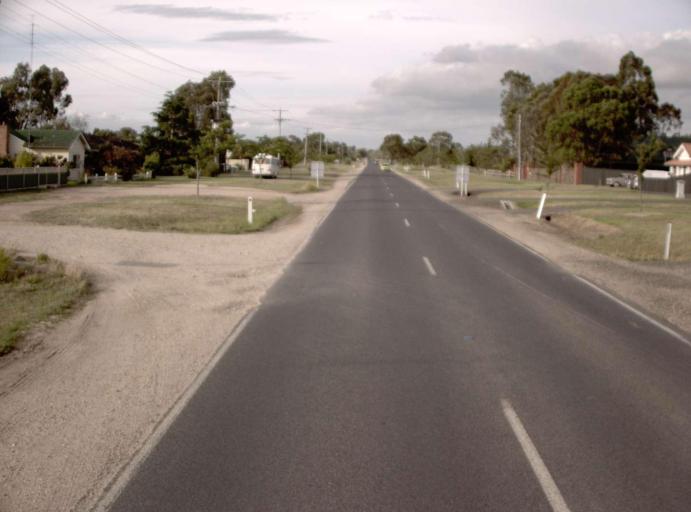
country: AU
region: Victoria
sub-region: Wellington
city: Sale
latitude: -37.9565
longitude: 146.9869
